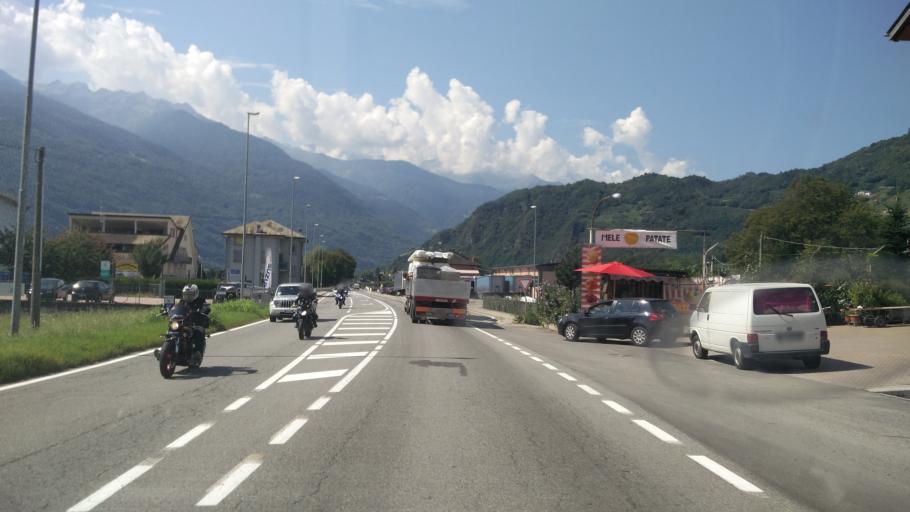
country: IT
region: Lombardy
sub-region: Provincia di Sondrio
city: Bianzone
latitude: 46.1811
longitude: 10.1138
